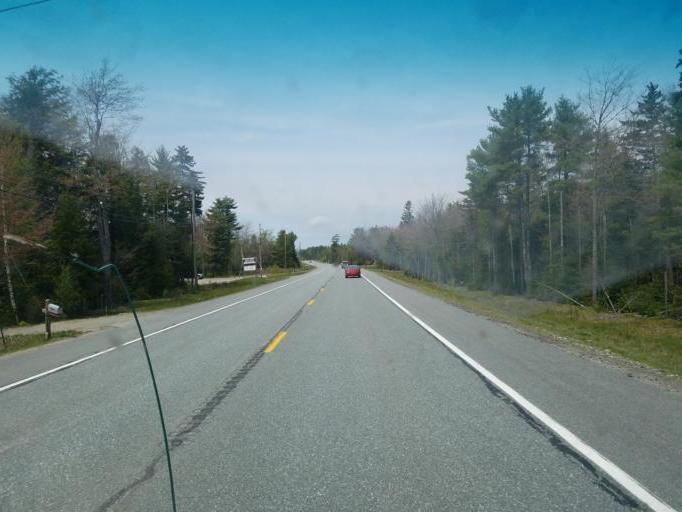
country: US
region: Maine
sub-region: Hancock County
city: Surry
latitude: 44.6067
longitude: -68.5182
